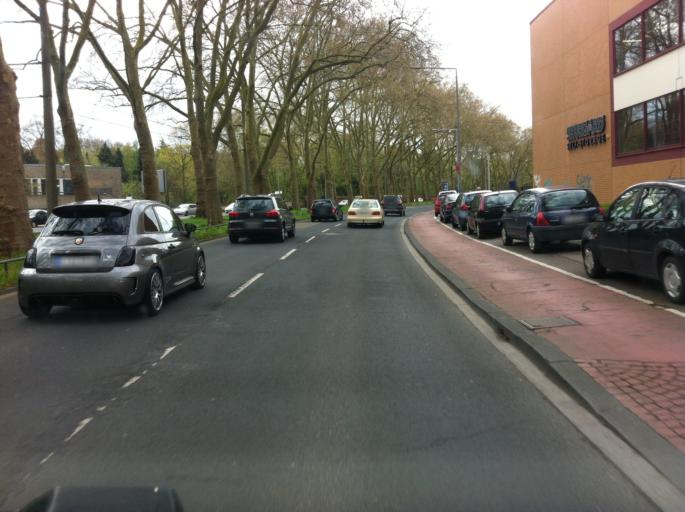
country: DE
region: North Rhine-Westphalia
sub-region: Regierungsbezirk Koln
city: Neuehrenfeld
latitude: 50.9428
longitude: 6.9126
